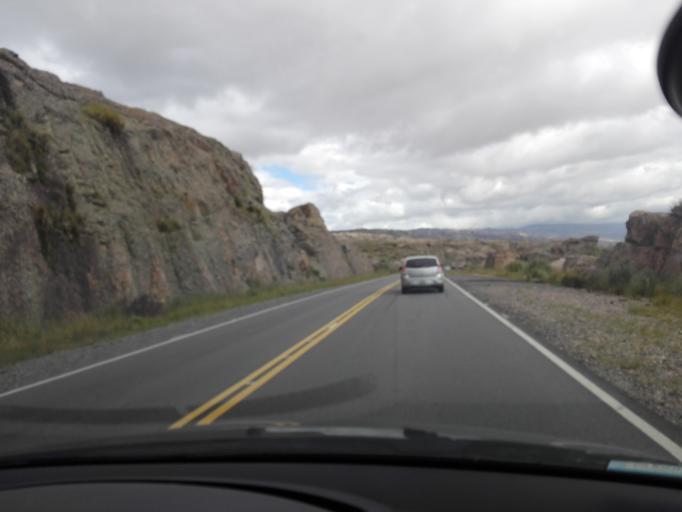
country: AR
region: Cordoba
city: Villa Cura Brochero
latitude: -31.6314
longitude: -64.9094
